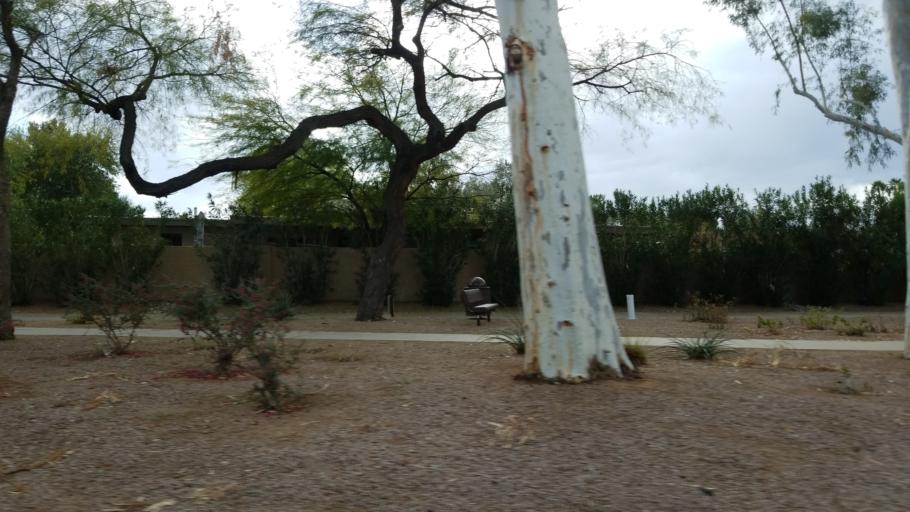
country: US
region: Arizona
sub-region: Maricopa County
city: Paradise Valley
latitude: 33.5600
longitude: -111.9088
